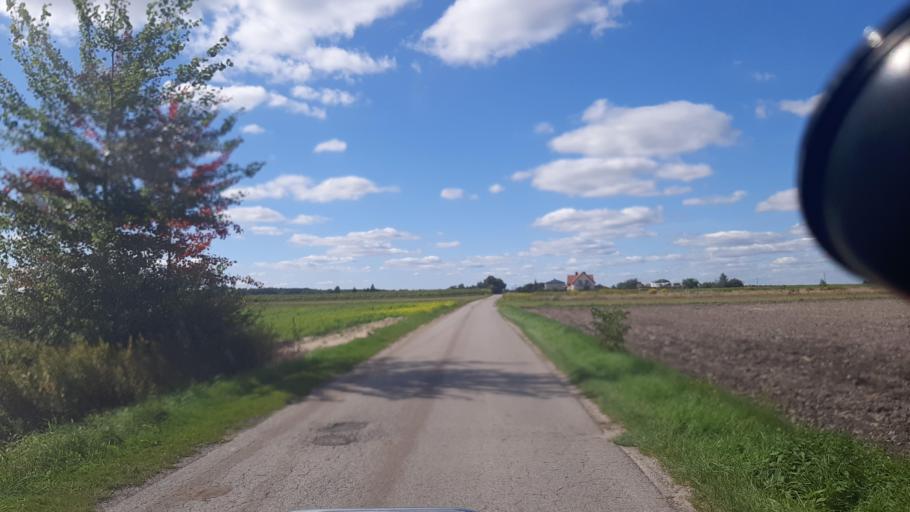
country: PL
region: Lublin Voivodeship
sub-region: Powiat lubartowski
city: Kamionka
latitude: 51.4048
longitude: 22.4080
